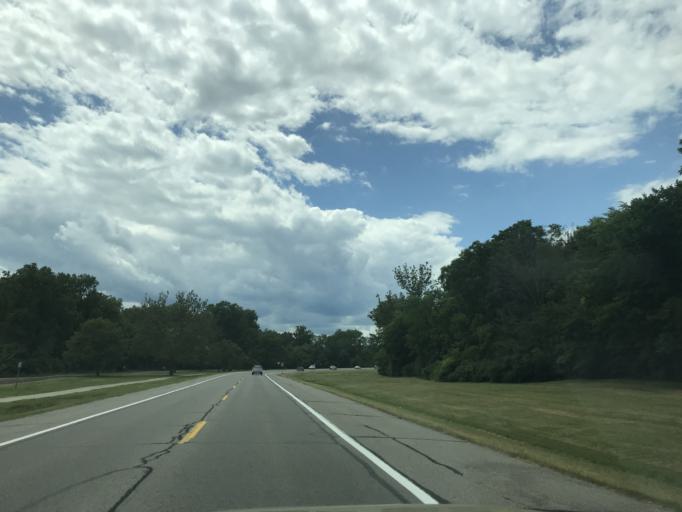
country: US
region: Michigan
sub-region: Wayne County
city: Dearborn Heights
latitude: 42.3474
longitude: -83.2850
